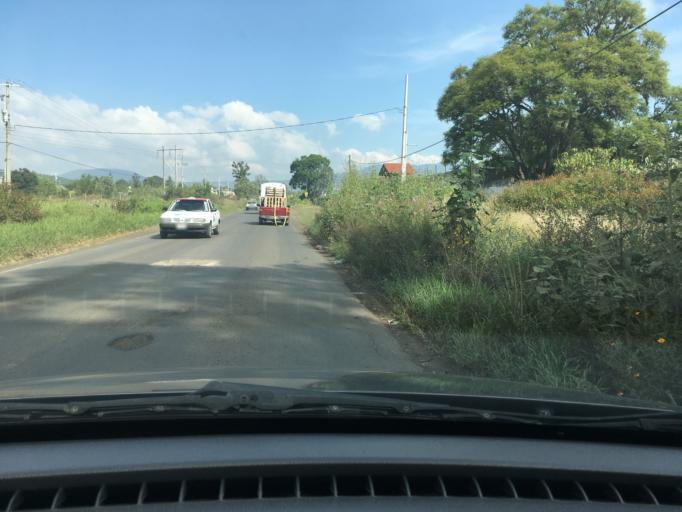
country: MX
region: Michoacan
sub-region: Morelia
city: La Mintzita (Piedra Dura)
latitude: 19.6408
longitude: -101.2775
